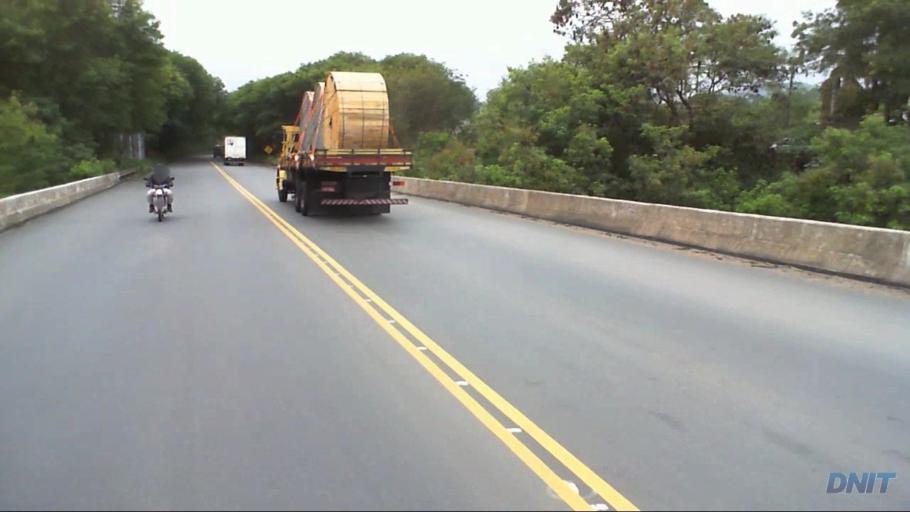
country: BR
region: Minas Gerais
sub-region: Coronel Fabriciano
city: Coronel Fabriciano
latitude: -19.5237
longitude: -42.6541
